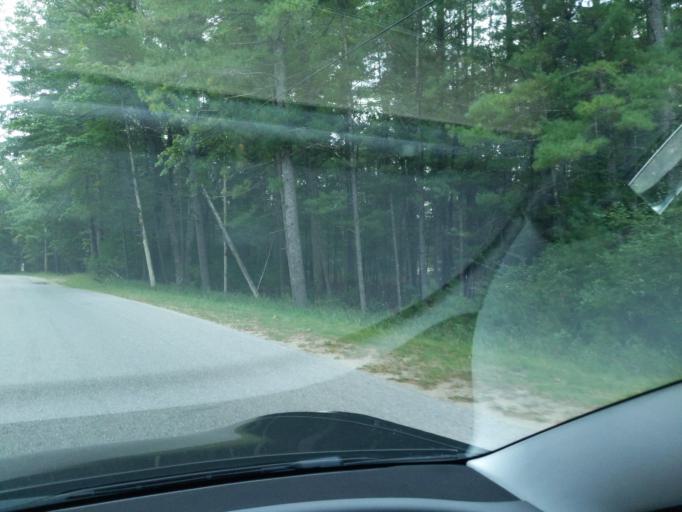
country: US
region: Michigan
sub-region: Kalkaska County
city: Rapid City
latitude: 44.8446
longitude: -85.3075
